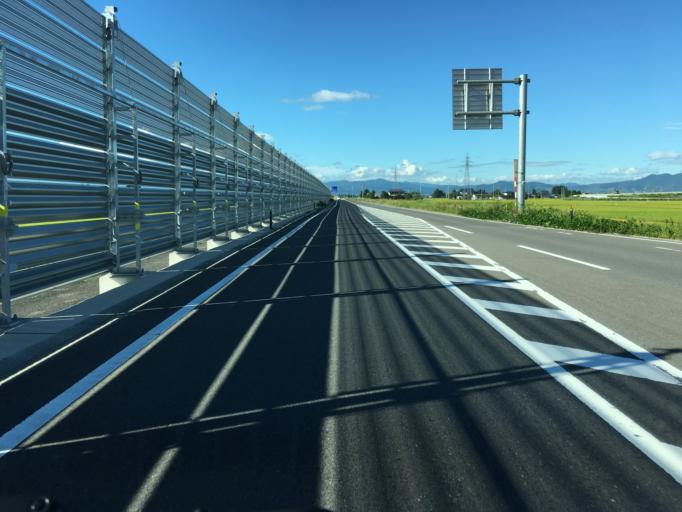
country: JP
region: Yamagata
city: Yonezawa
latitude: 37.9513
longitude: 140.1123
